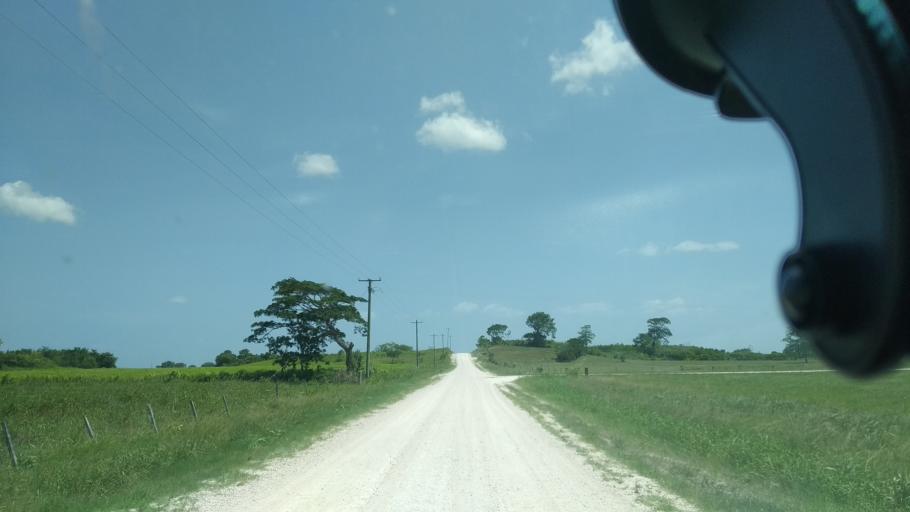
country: BZ
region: Cayo
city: San Ignacio
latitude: 17.3082
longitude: -89.0480
